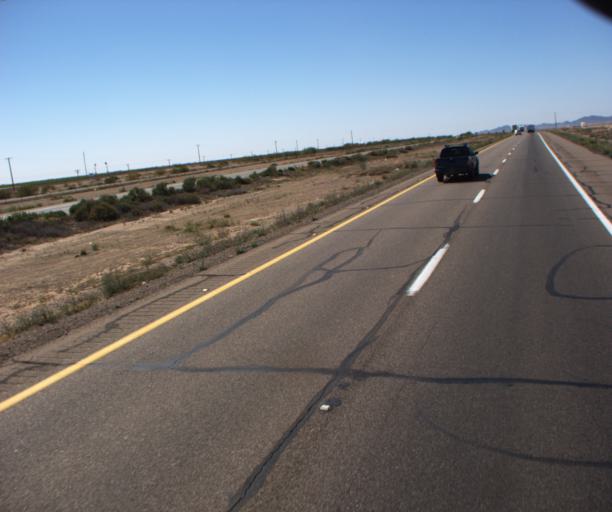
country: US
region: Arizona
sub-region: Maricopa County
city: Gila Bend
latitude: 32.9281
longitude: -112.8387
